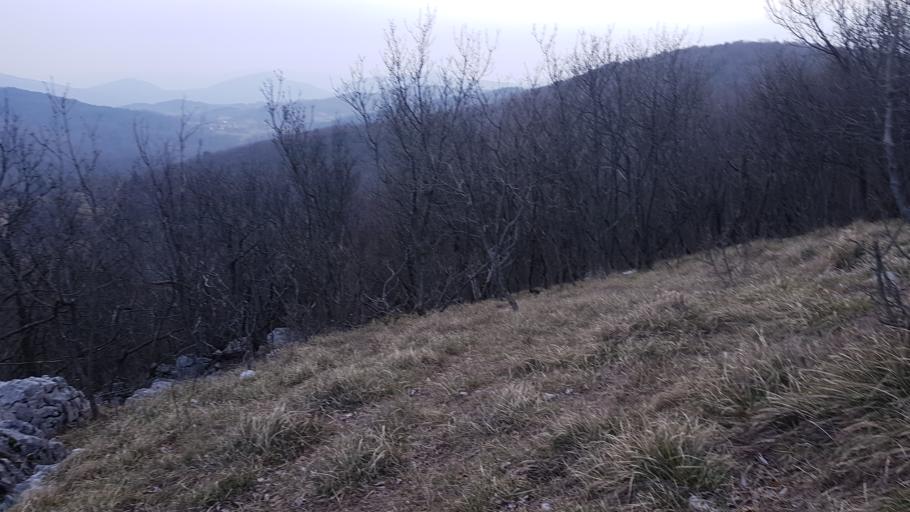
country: SI
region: Kanal
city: Kanal
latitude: 46.0552
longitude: 13.6618
